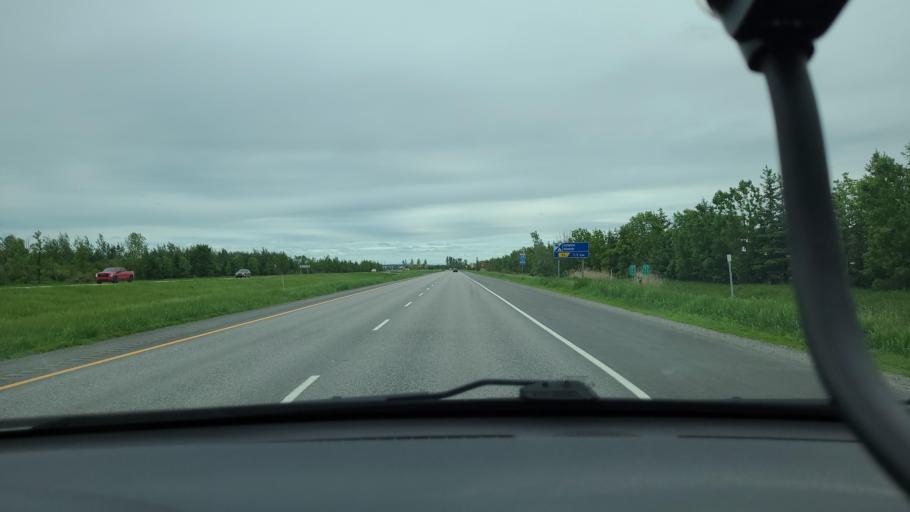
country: CA
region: Quebec
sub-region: Lanaudiere
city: Saint-Jacques
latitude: 45.8689
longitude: -73.6492
